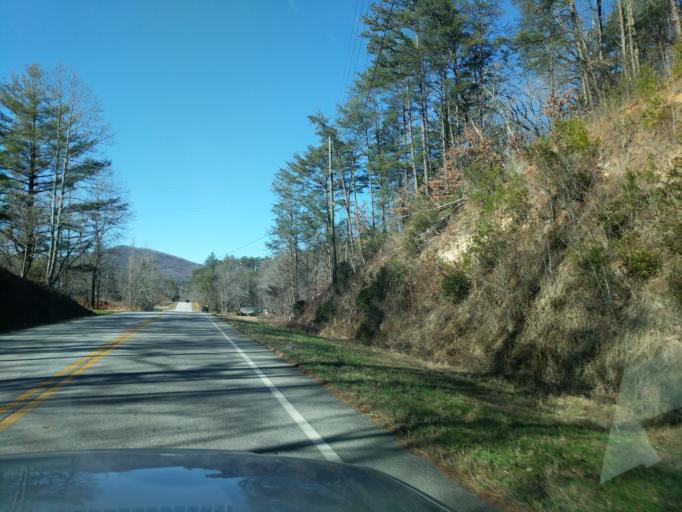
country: US
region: Georgia
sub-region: Rabun County
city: Clayton
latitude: 34.8442
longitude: -83.3486
